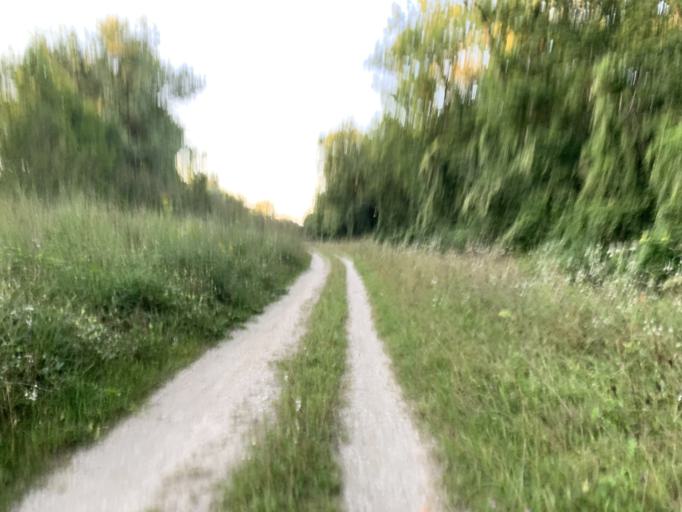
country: DE
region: Bavaria
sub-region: Upper Bavaria
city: Freising
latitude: 48.3860
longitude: 11.7486
